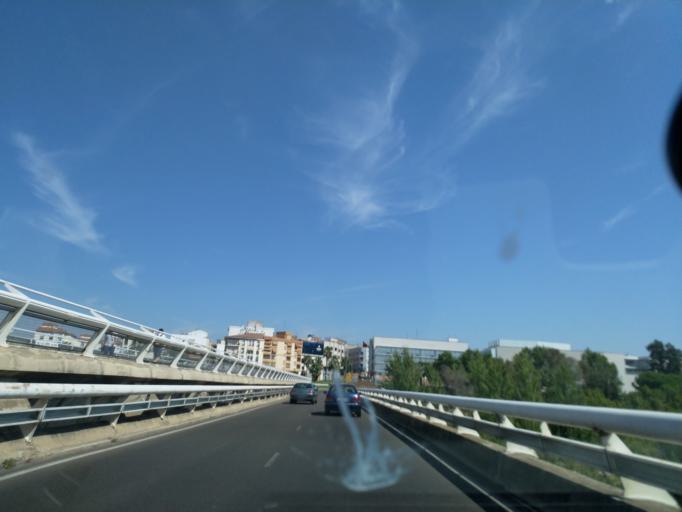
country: ES
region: Extremadura
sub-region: Provincia de Badajoz
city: Merida
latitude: 38.9171
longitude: -6.3524
